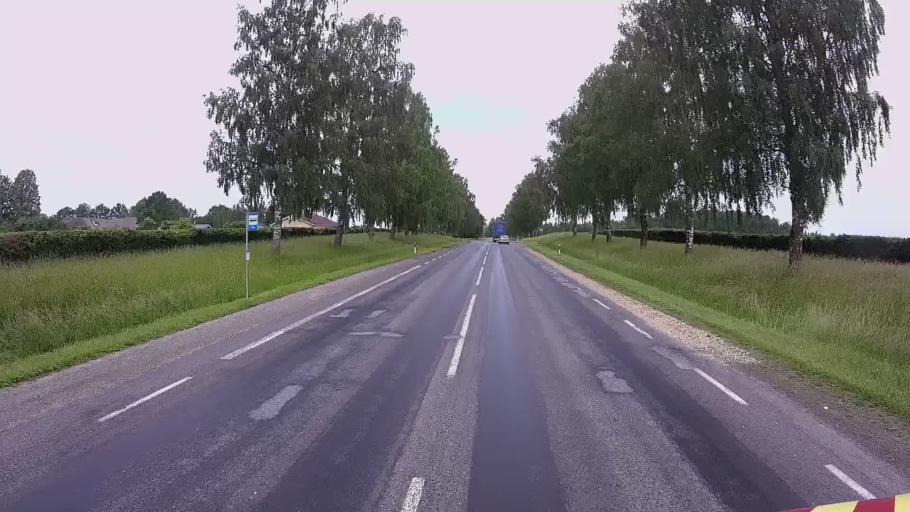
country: EE
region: Viljandimaa
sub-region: Viljandi linn
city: Viljandi
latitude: 58.3075
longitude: 25.5734
